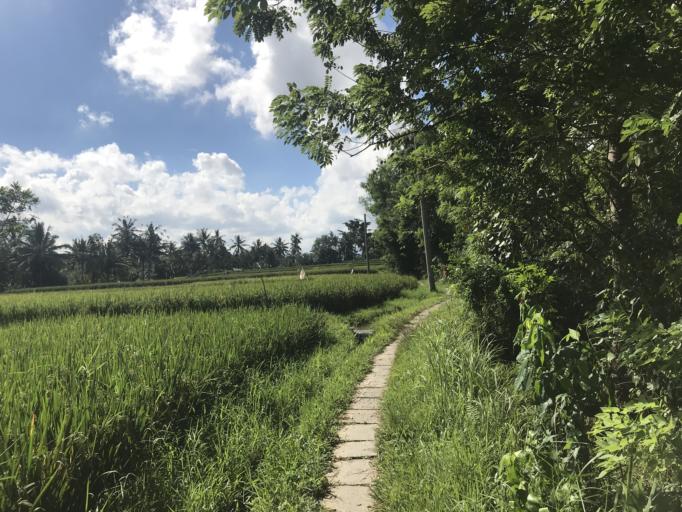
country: ID
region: Bali
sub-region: Kabupaten Gianyar
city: Ubud
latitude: -8.4895
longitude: 115.2617
